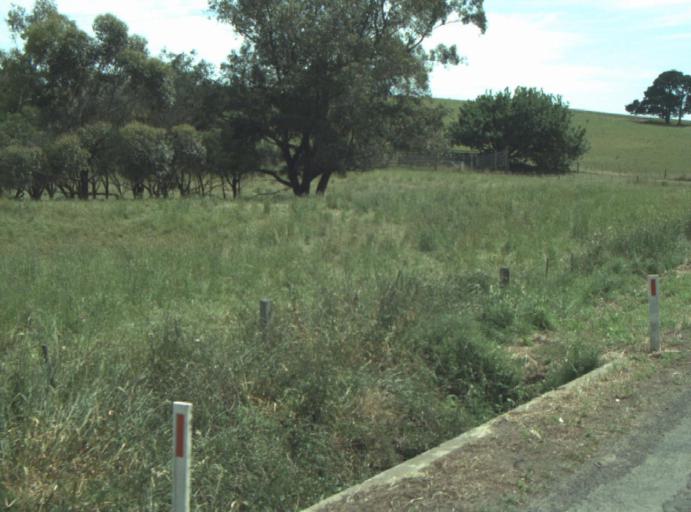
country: AU
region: Victoria
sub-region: Greater Geelong
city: Clifton Springs
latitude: -38.1482
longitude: 144.5952
